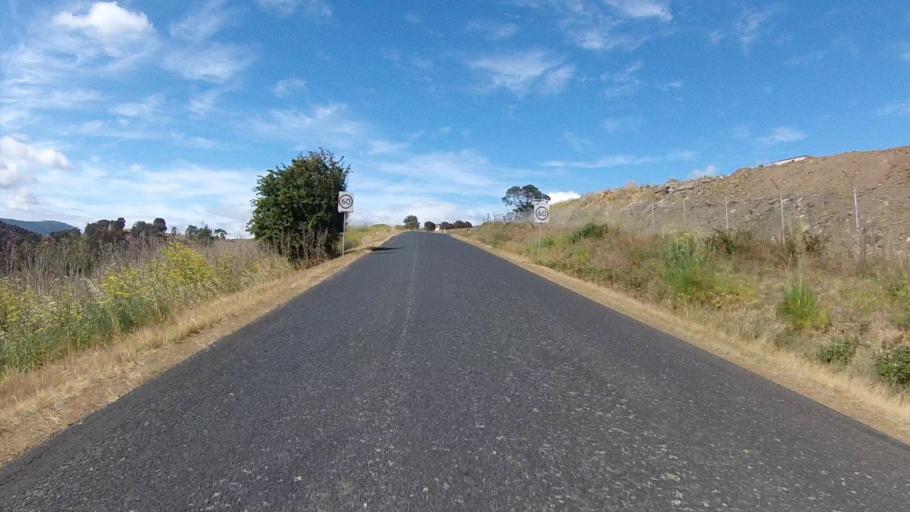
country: AU
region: Tasmania
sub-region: Brighton
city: Bridgewater
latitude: -42.7343
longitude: 147.2602
